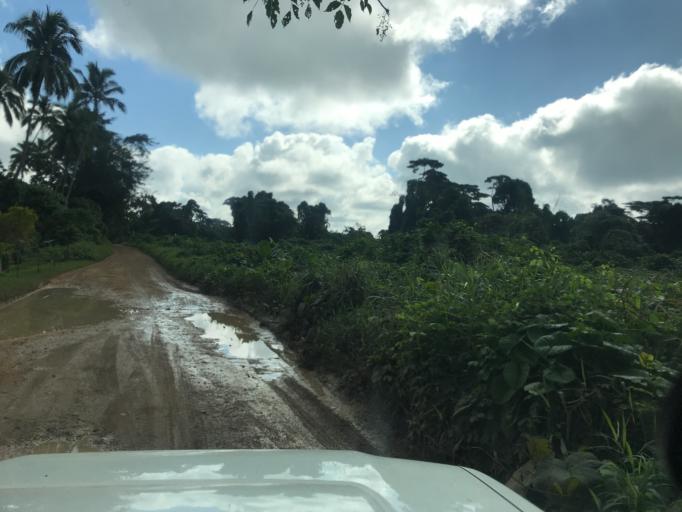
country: VU
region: Sanma
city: Luganville
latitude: -15.4946
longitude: 167.0894
